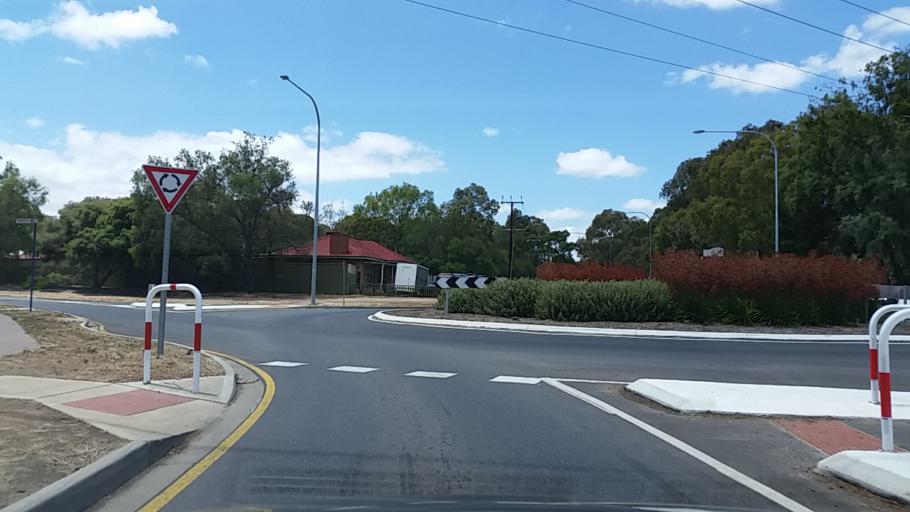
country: AU
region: South Australia
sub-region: Salisbury
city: Salisbury
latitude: -34.7665
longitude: 138.6055
